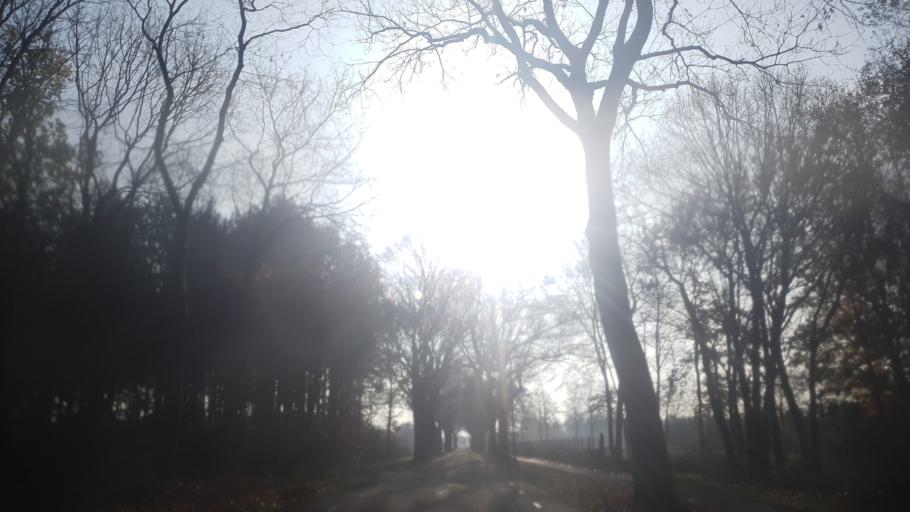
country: NL
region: North Brabant
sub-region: Gemeente Landerd
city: Reek
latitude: 51.7230
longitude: 5.6831
